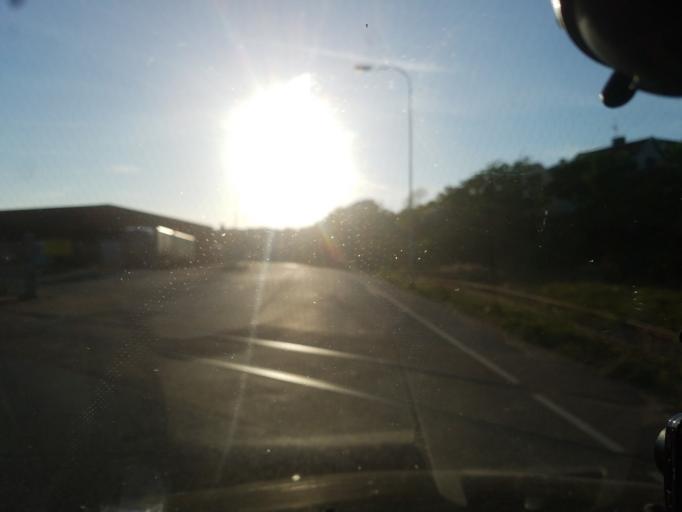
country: SE
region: Vaestra Goetaland
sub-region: Lysekils Kommun
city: Lysekil
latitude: 58.2766
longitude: 11.4520
